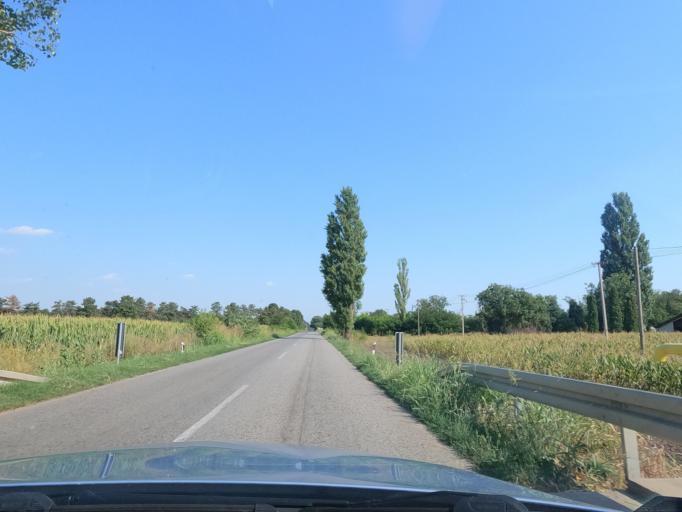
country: RS
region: Autonomna Pokrajina Vojvodina
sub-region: Juznobacki Okrug
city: Becej
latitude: 45.6329
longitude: 20.0127
